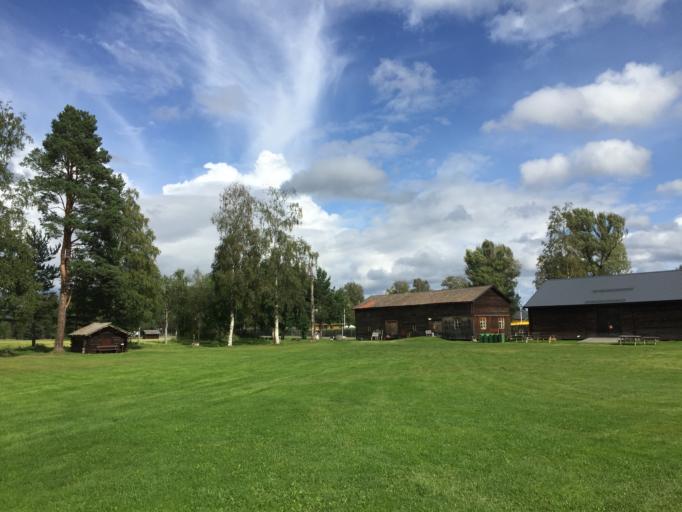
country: SE
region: Gaevleborg
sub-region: Ljusdals Kommun
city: Ljusdal
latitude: 61.8201
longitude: 16.0766
